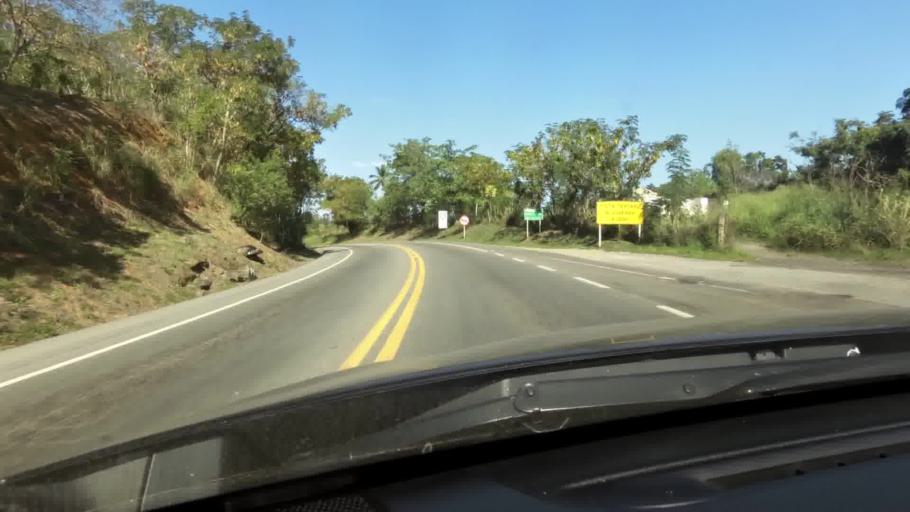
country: BR
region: Espirito Santo
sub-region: Cachoeiro De Itapemirim
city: Cachoeiro de Itapemirim
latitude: -20.9214
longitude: -41.0782
